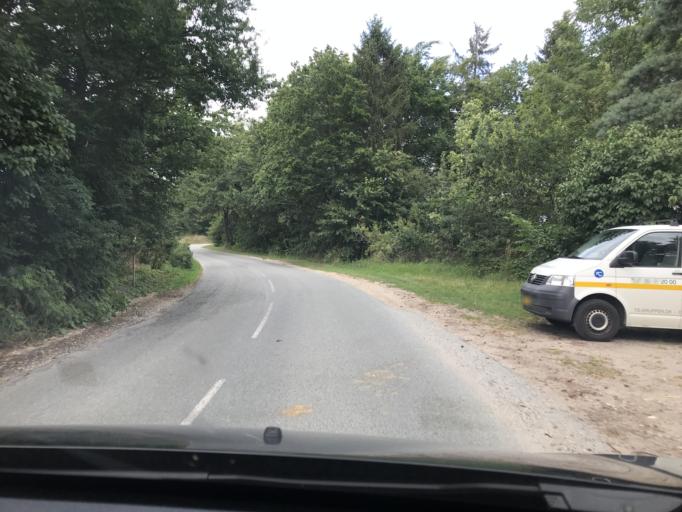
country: DK
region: Central Jutland
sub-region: Syddjurs Kommune
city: Ronde
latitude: 56.3534
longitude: 10.4501
